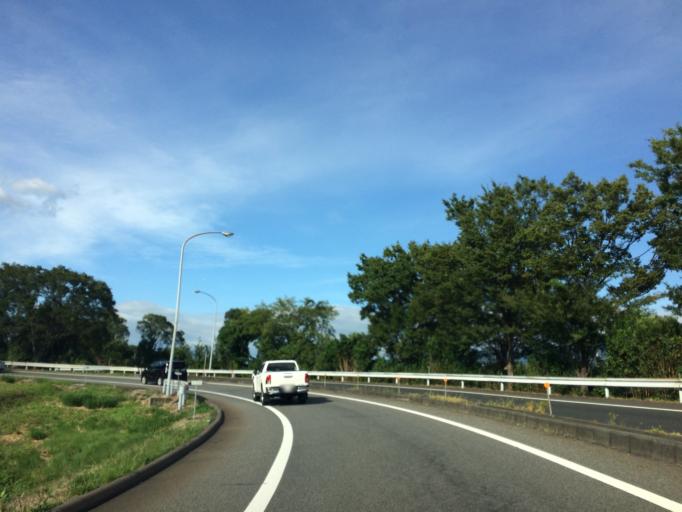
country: JP
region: Gunma
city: Shibukawa
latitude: 36.4752
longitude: 139.0168
